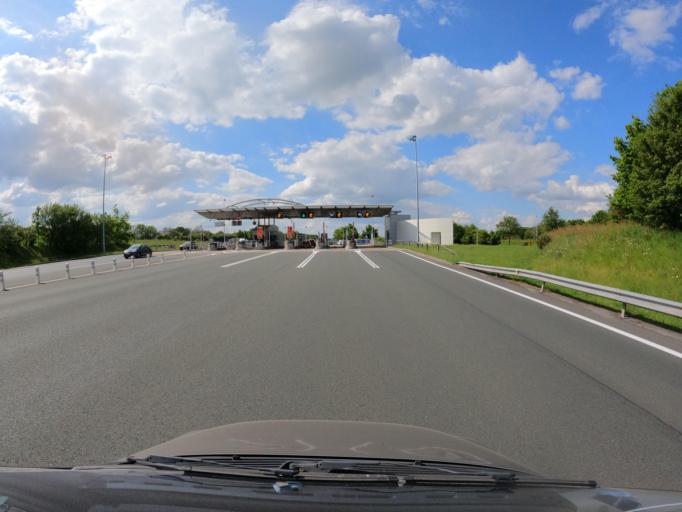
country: FR
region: Pays de la Loire
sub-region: Departement de Maine-et-Loire
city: La Tessoualle
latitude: 47.0186
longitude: -0.8800
